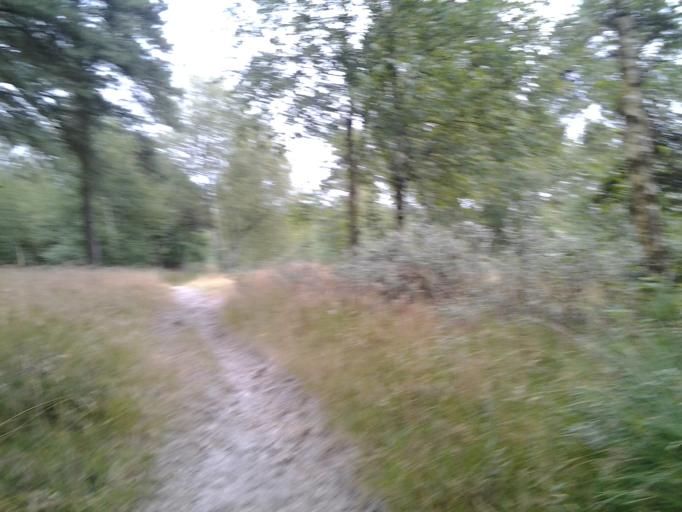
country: DE
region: Schleswig-Holstein
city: List
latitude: 55.1170
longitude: 8.5302
